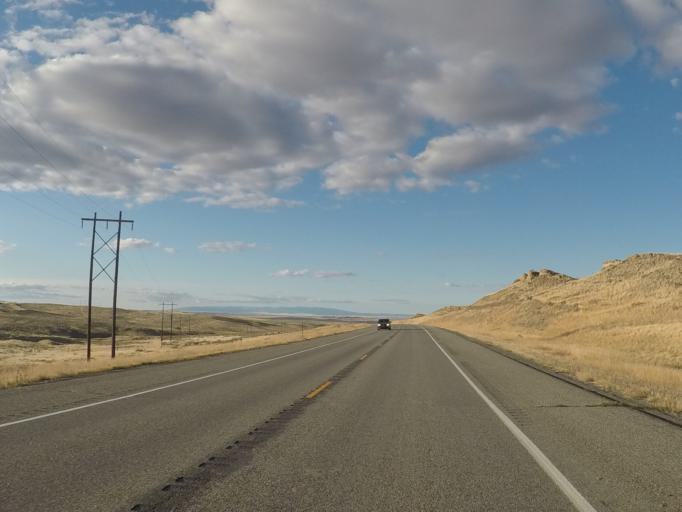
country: US
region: Montana
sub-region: Golden Valley County
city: Ryegate
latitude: 46.1451
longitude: -108.8927
